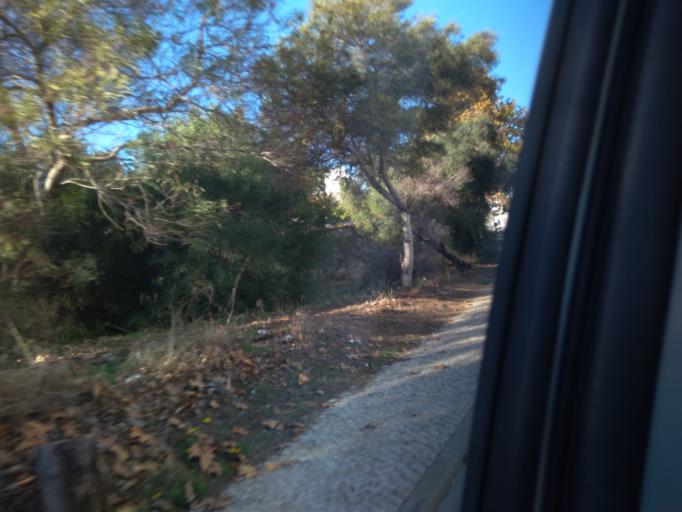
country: PT
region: Faro
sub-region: Albufeira
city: Albufeira
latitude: 37.0997
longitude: -8.2245
